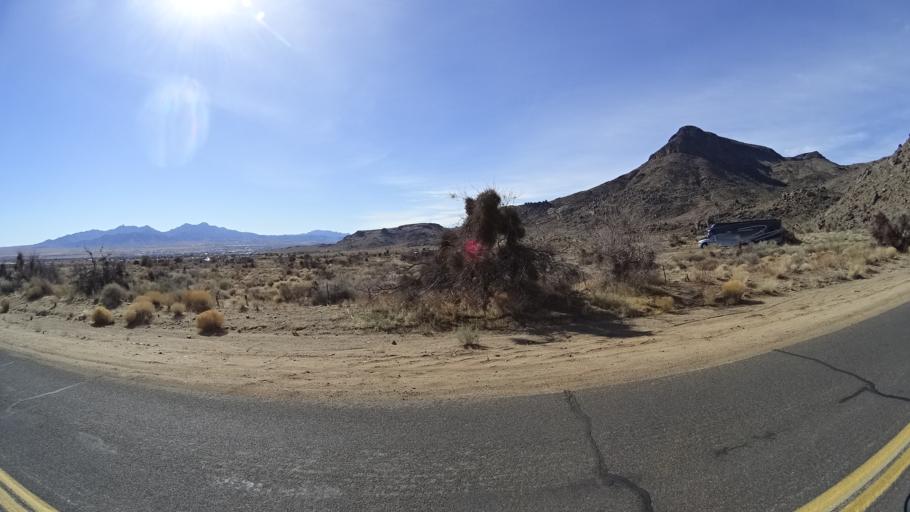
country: US
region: Arizona
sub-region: Mohave County
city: New Kingman-Butler
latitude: 35.2877
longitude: -114.0566
